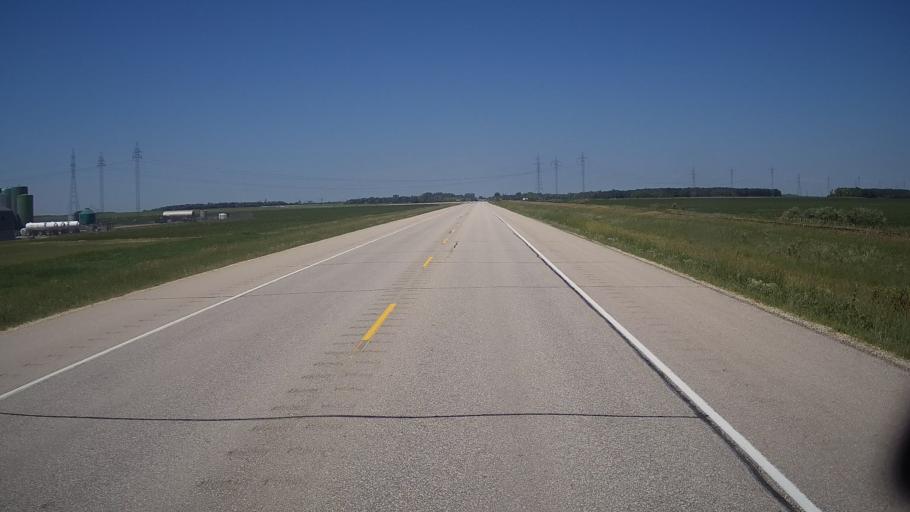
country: CA
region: Manitoba
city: Stonewall
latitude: 50.0496
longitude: -97.4200
